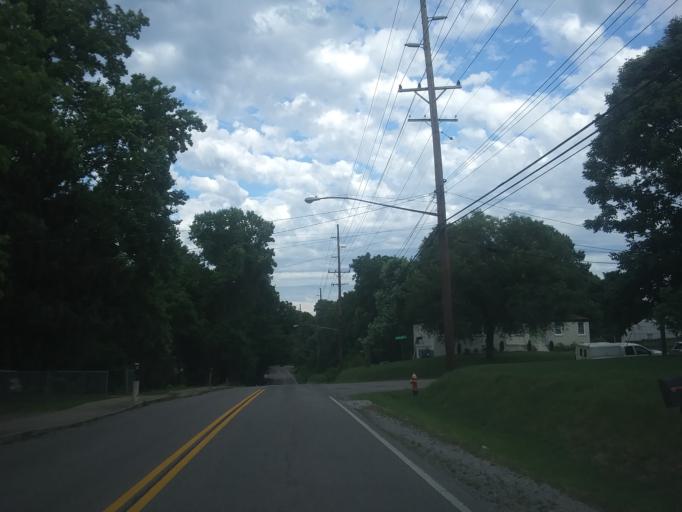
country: US
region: Tennessee
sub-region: Davidson County
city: Oak Hill
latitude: 36.0983
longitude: -86.7259
